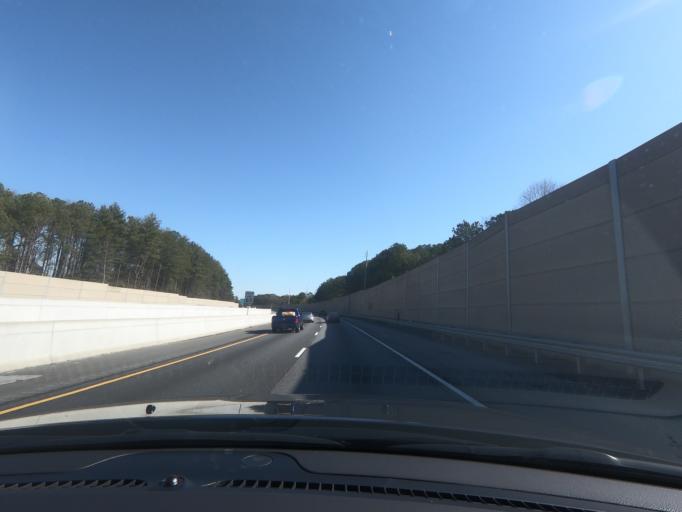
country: US
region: Georgia
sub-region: Cherokee County
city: Woodstock
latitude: 34.0550
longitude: -84.5456
